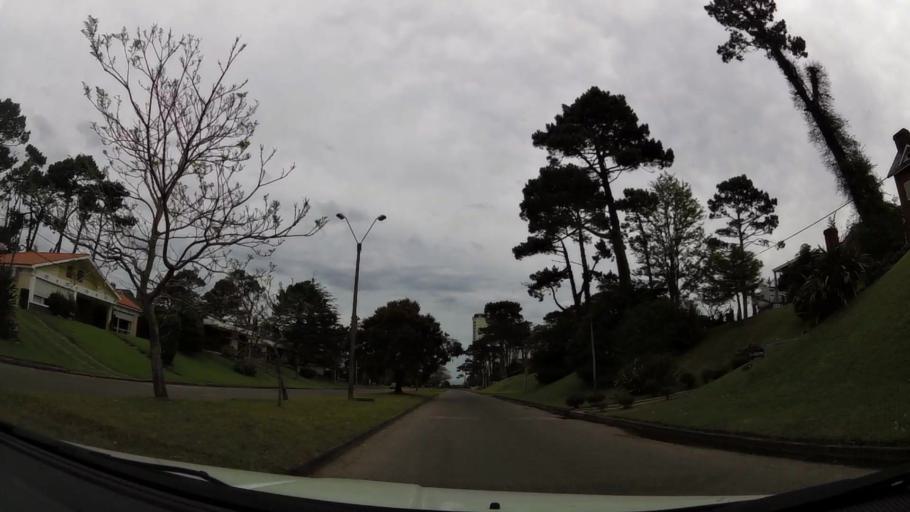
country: UY
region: Maldonado
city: Maldonado
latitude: -34.9285
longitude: -54.9509
